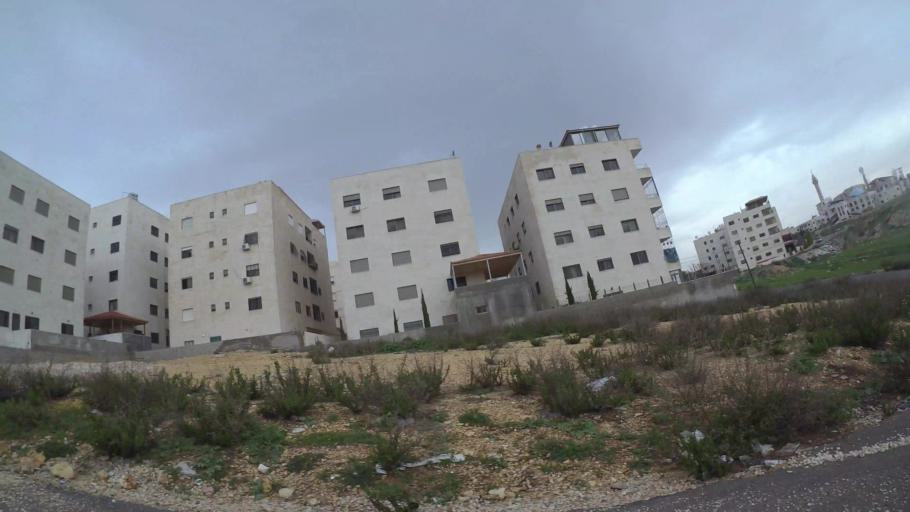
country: JO
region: Amman
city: Umm as Summaq
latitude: 31.9029
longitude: 35.8359
